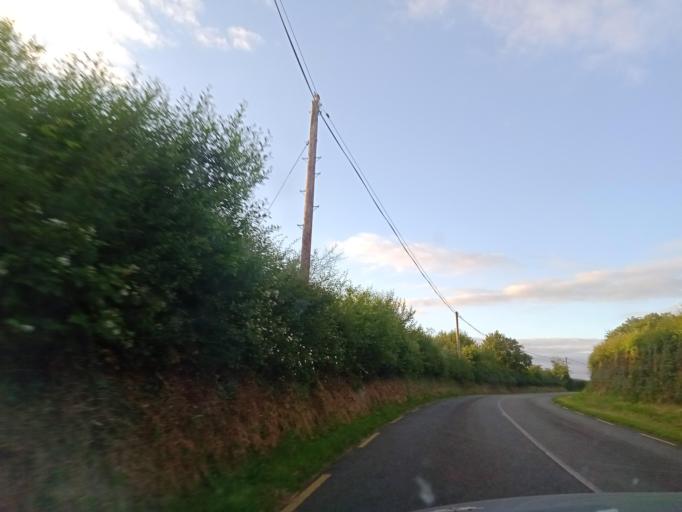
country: IE
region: Leinster
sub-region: Kilkenny
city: Castlecomer
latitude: 52.8534
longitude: -7.1732
